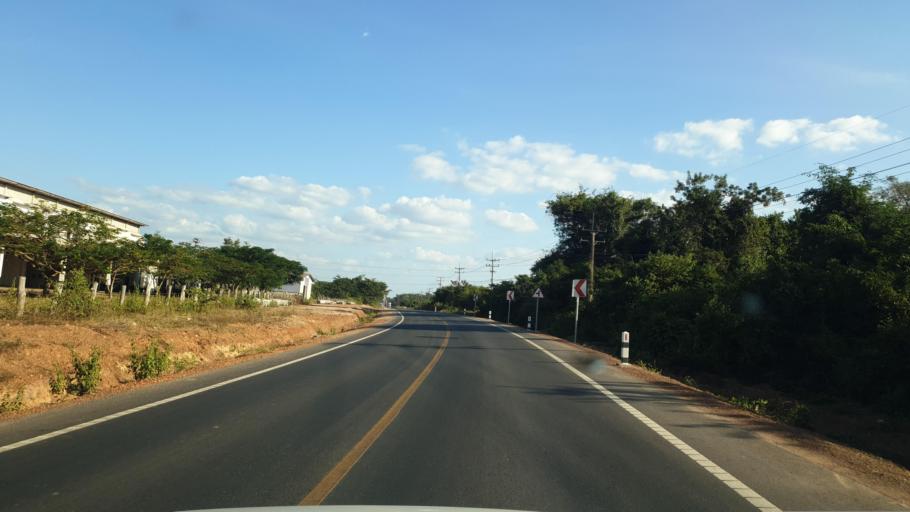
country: LA
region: Khammouan
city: Muang Hinboun
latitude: 17.6069
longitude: 104.6762
